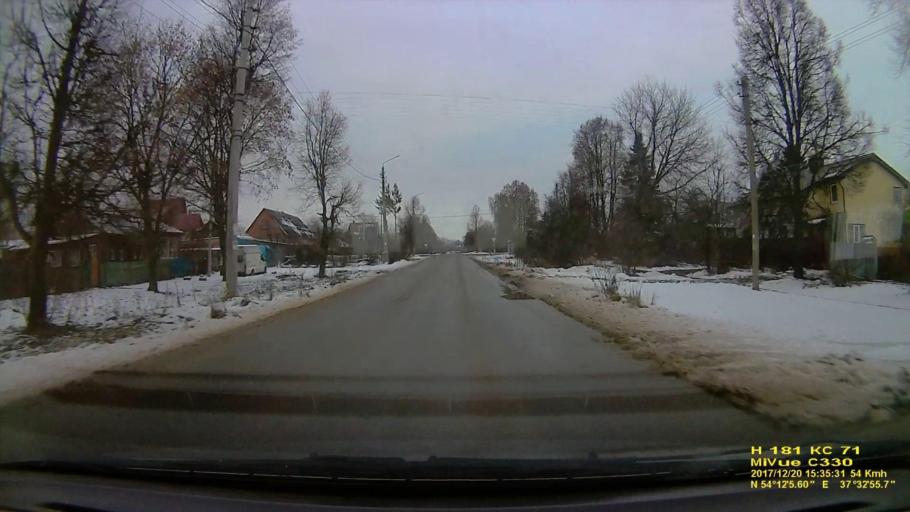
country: RU
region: Tula
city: Tula
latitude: 54.2014
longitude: 37.5489
